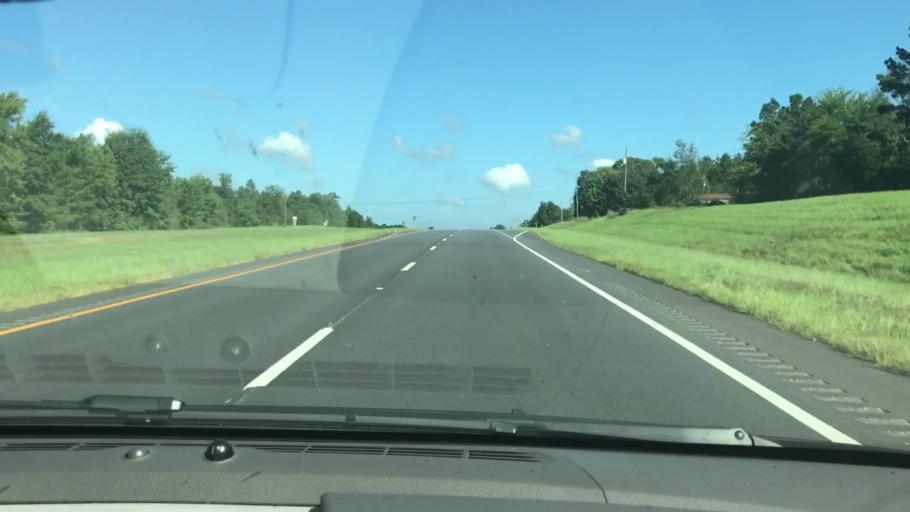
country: US
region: Alabama
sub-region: Barbour County
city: Eufaula
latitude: 32.0369
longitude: -85.1254
